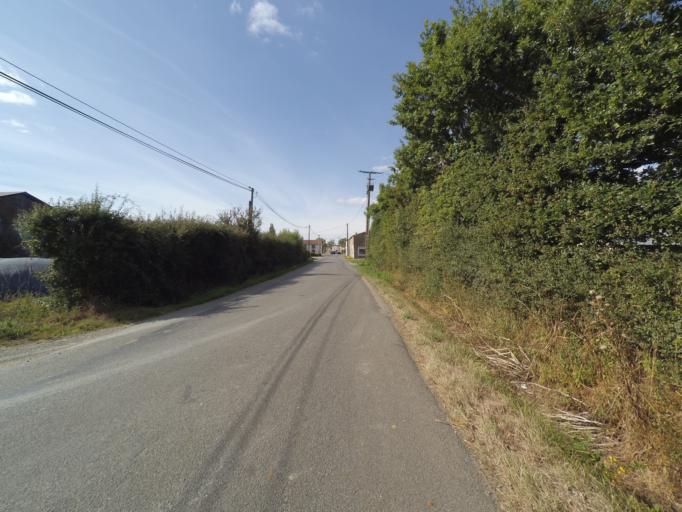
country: FR
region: Pays de la Loire
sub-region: Departement de la Loire-Atlantique
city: Vieillevigne
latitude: 46.9593
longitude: -1.4560
